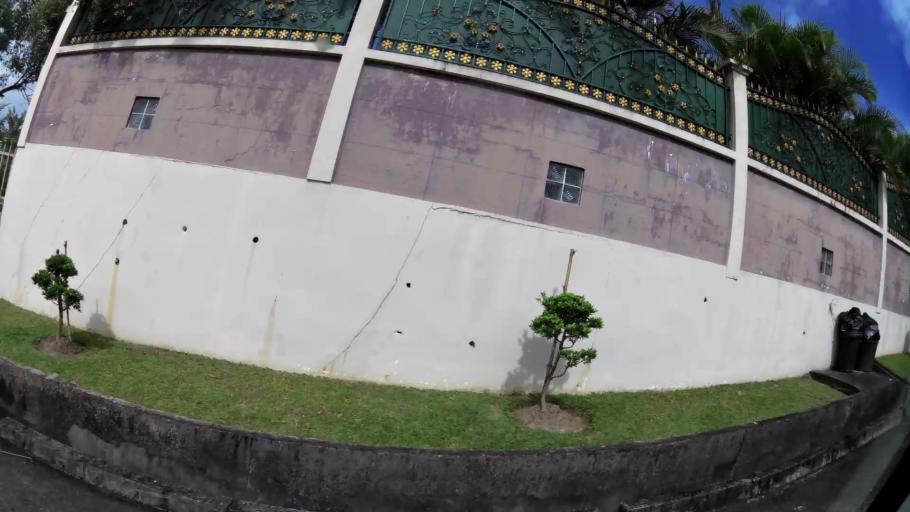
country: BN
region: Brunei and Muara
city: Bandar Seri Begawan
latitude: 4.8908
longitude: 114.8959
